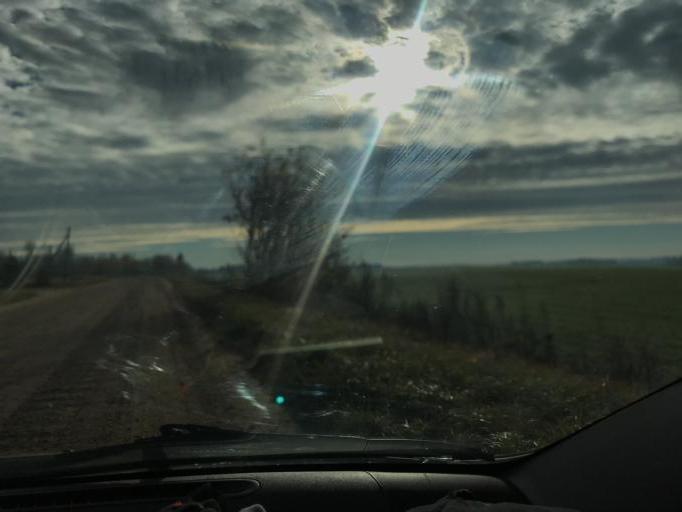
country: BY
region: Vitebsk
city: Haradok
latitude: 55.4552
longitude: 30.0142
